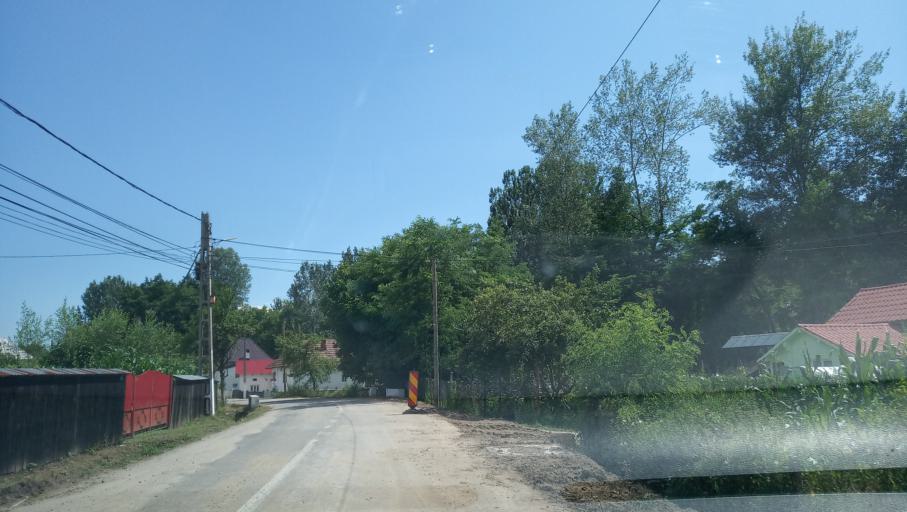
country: RO
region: Valcea
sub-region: Comuna Barbatesti
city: Bodesti
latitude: 45.1405
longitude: 24.1453
